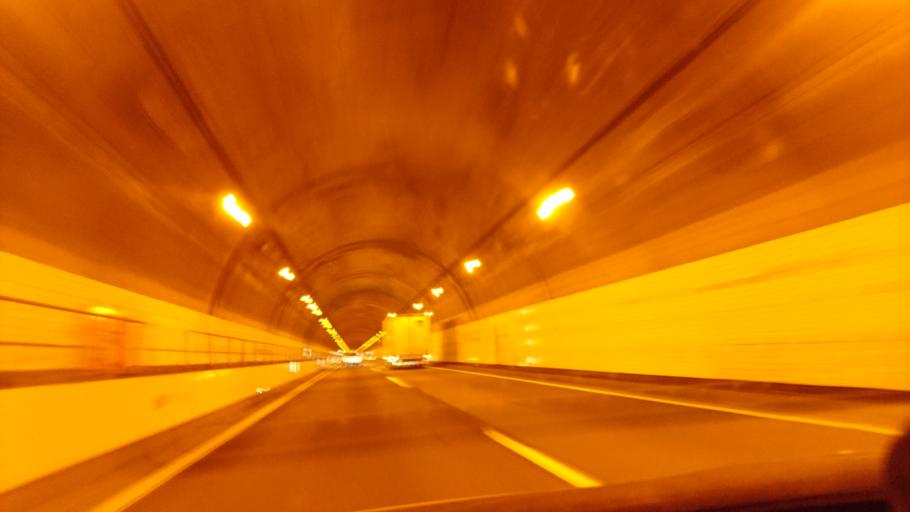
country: JP
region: Iwate
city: Ichinoseki
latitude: 38.9512
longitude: 141.1057
